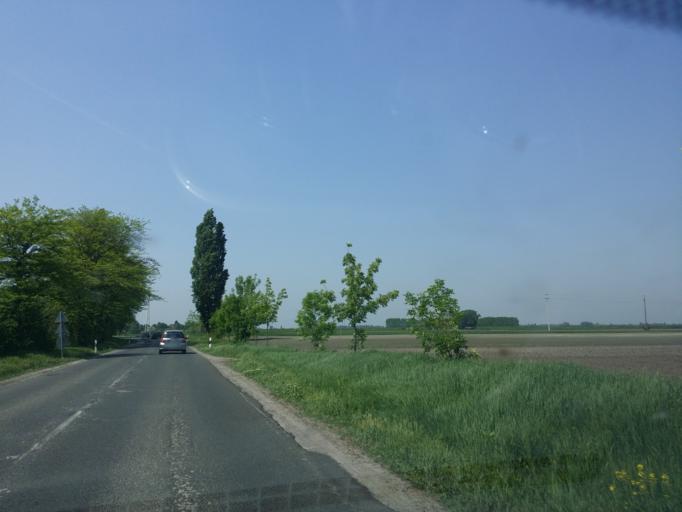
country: HU
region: Pest
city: Kiskunlachaza
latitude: 47.1735
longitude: 18.9868
